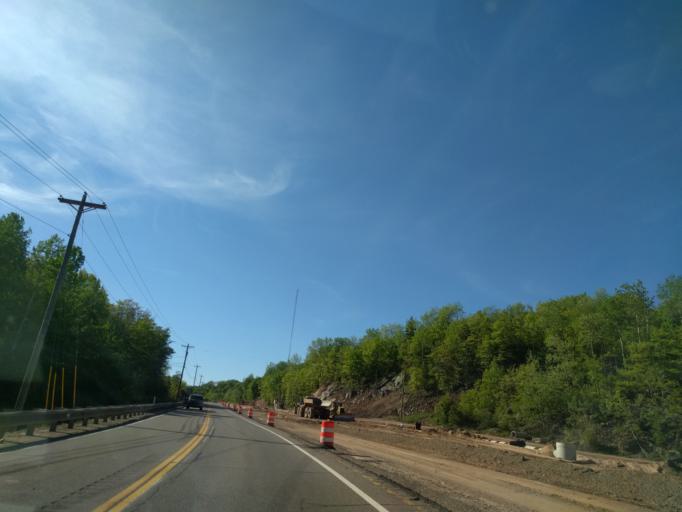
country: US
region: Michigan
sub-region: Marquette County
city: Marquette
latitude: 46.4945
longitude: -87.4137
